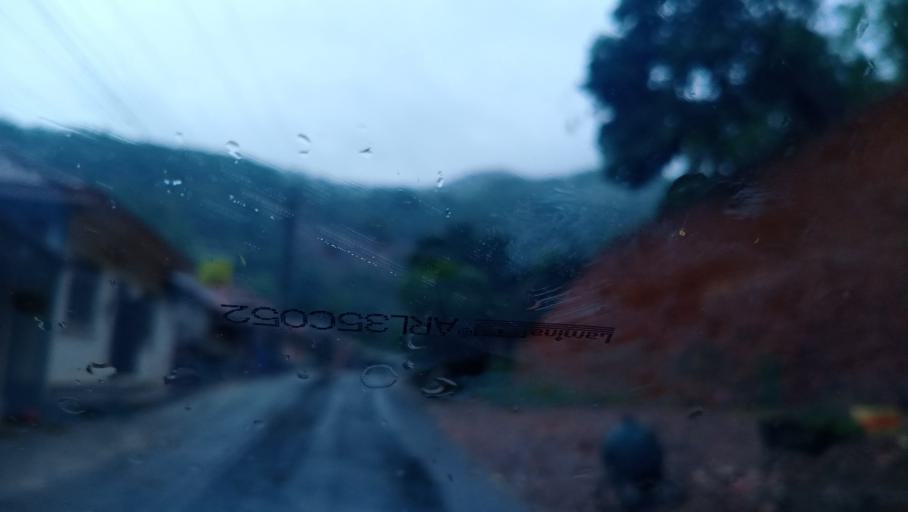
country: LA
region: Phongsali
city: Khoa
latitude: 21.0757
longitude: 102.5017
